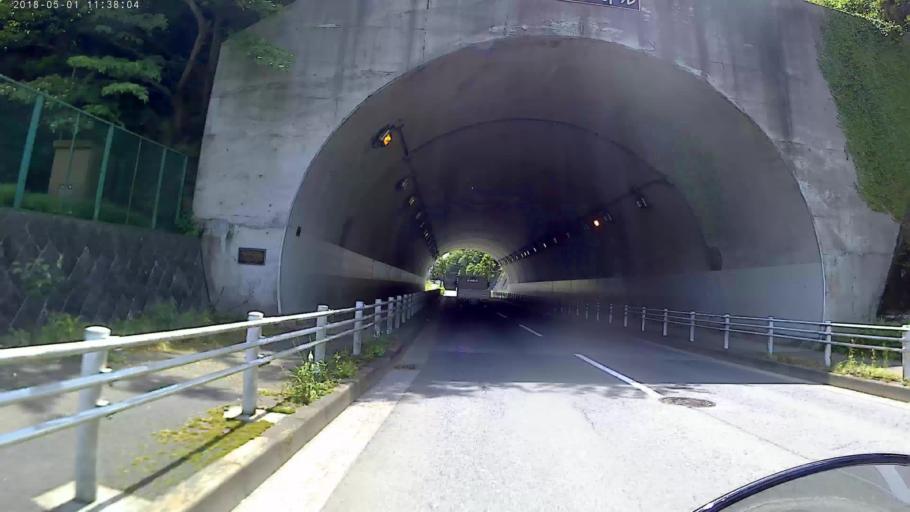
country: JP
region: Kanagawa
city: Minami-rinkan
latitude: 35.5109
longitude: 139.4903
